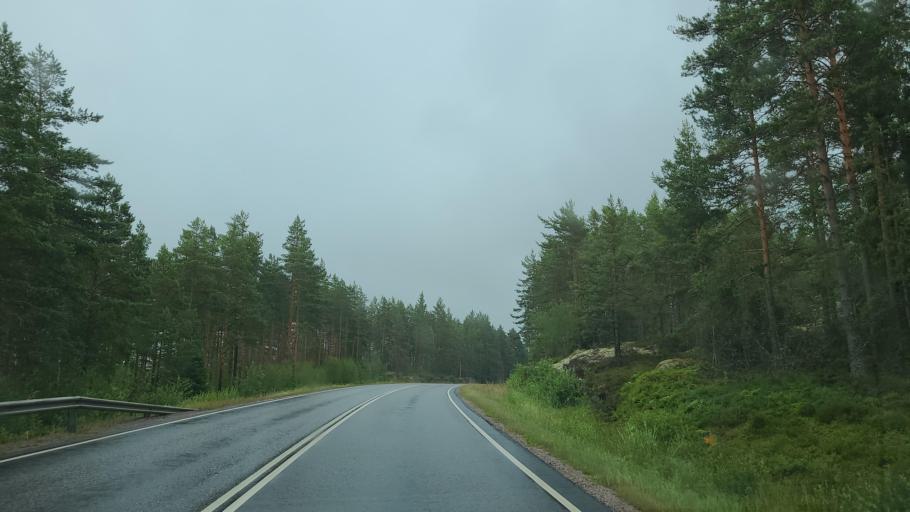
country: FI
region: Varsinais-Suomi
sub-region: Aboland-Turunmaa
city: Kimito
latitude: 60.2229
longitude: 22.6296
